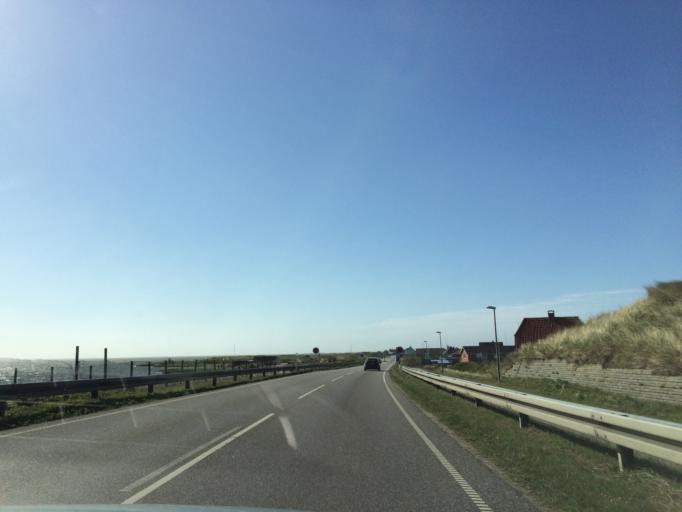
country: DK
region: Central Jutland
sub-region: Ringkobing-Skjern Kommune
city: Hvide Sande
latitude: 55.9879
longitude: 8.1352
